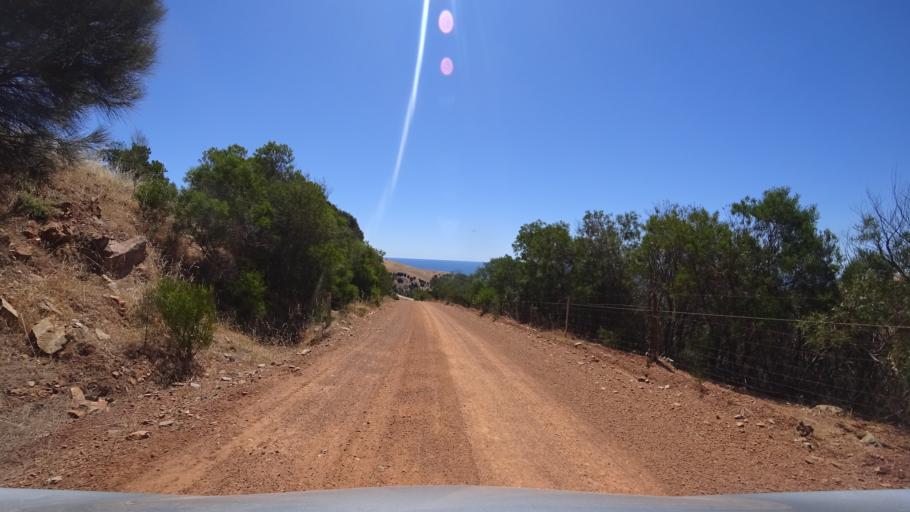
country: AU
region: South Australia
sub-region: Kangaroo Island
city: Kingscote
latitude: -35.6779
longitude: 136.9757
